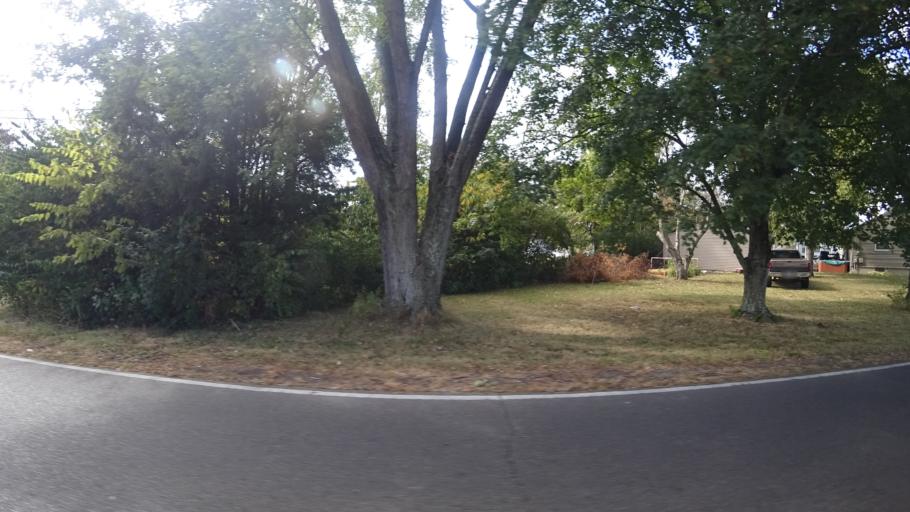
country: US
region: Ohio
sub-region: Butler County
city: Fairfield
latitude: 39.3610
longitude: -84.5446
